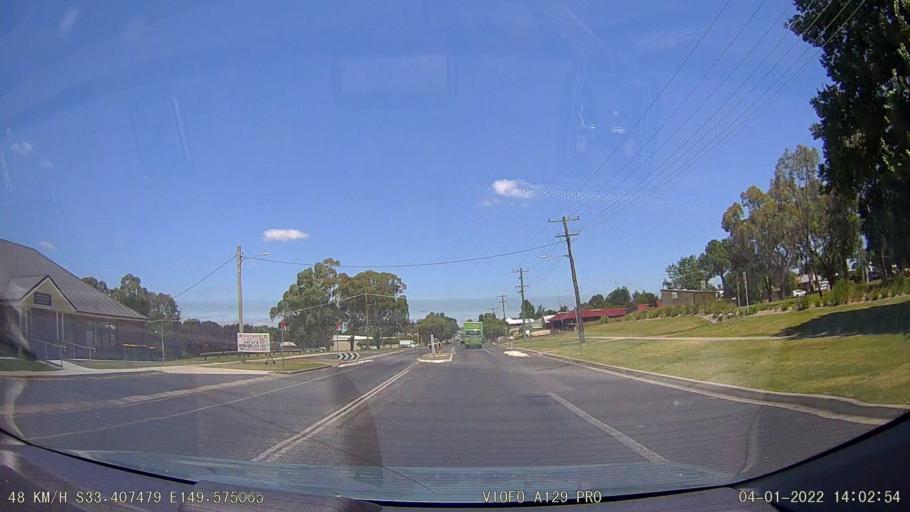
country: AU
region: New South Wales
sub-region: Bathurst Regional
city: Bathurst
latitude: -33.4073
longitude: 149.5750
